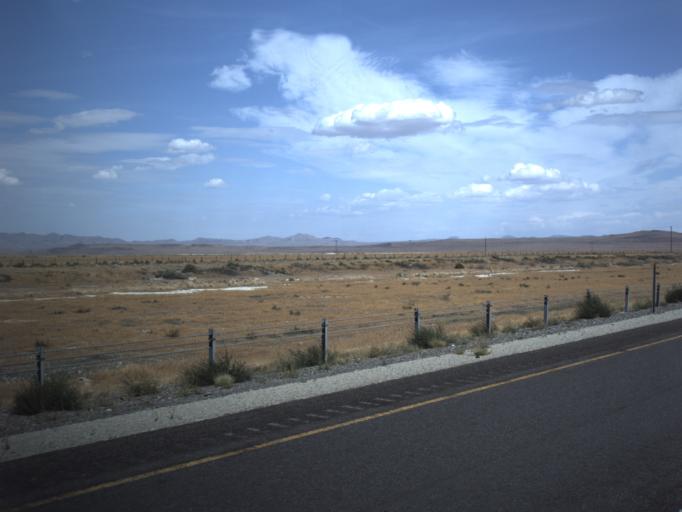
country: US
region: Utah
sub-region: Tooele County
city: Grantsville
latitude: 40.7262
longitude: -113.2396
